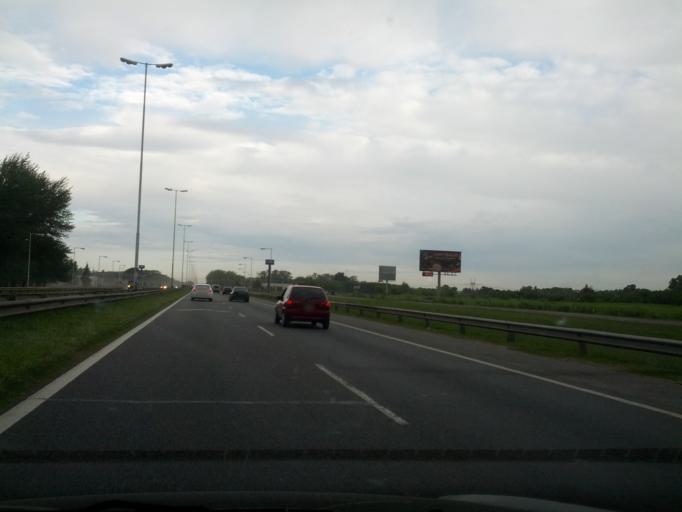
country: AR
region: Buenos Aires
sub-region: Partido de General Rodriguez
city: General Rodriguez
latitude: -34.5848
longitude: -58.9861
